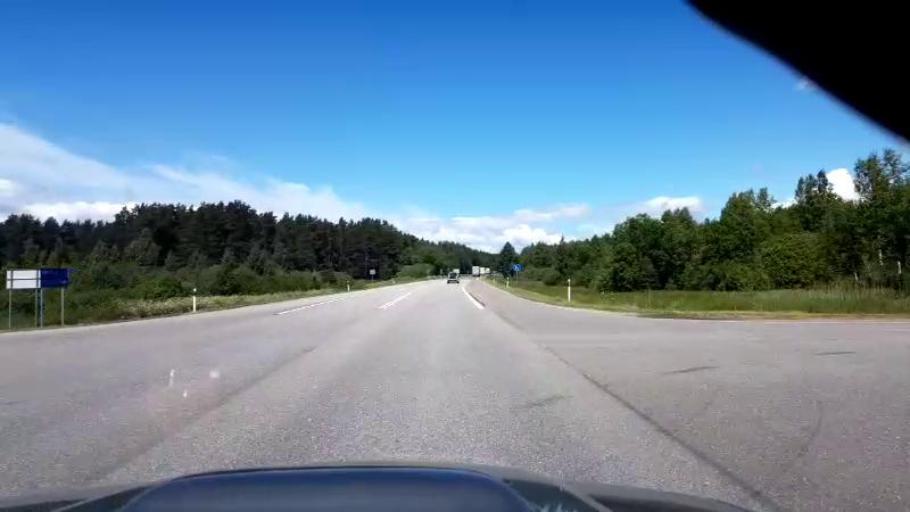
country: LV
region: Salacgrivas
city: Ainazi
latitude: 58.0884
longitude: 24.5082
